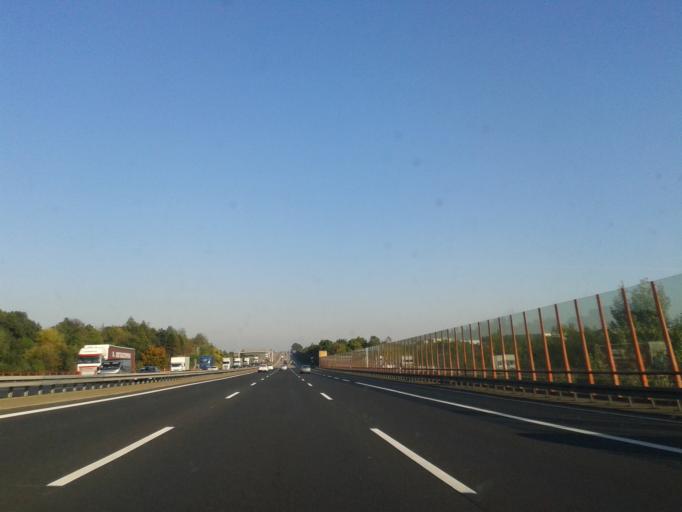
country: DE
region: Saxony
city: Wilsdruff
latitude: 51.0605
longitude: 13.5271
